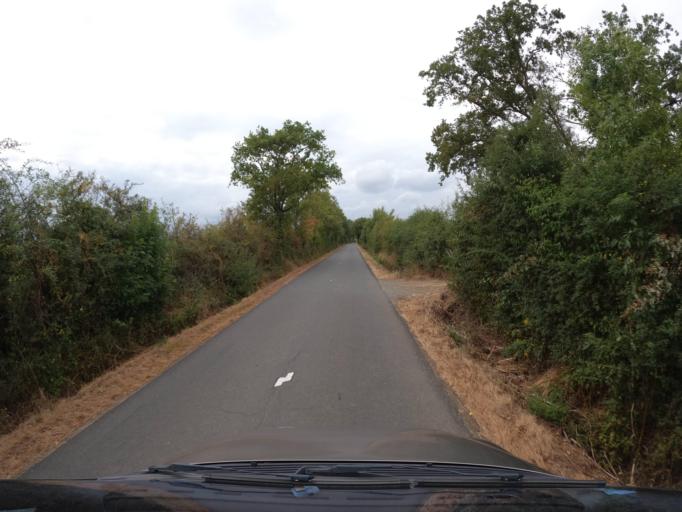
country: FR
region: Pays de la Loire
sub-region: Departement de Maine-et-Loire
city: Saint-Christophe-du-Bois
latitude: 47.0438
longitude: -0.9813
